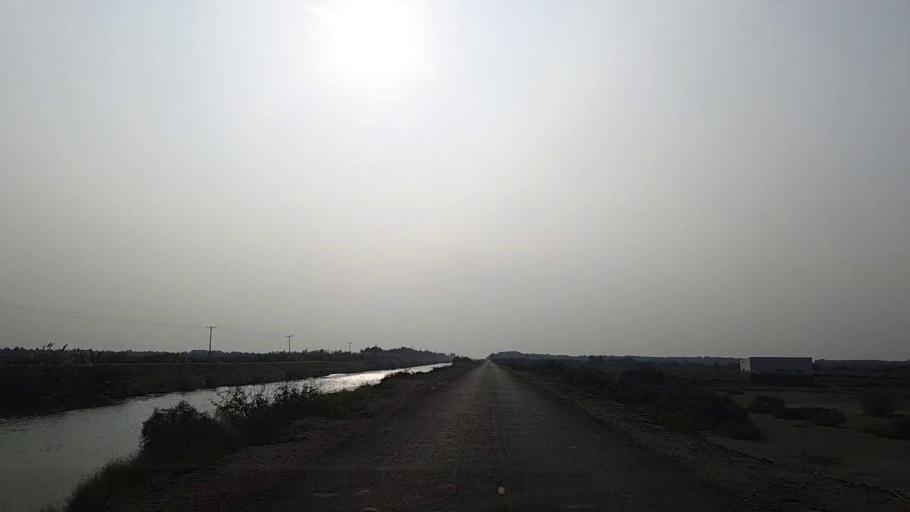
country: PK
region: Sindh
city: Mirpur Sakro
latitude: 24.6296
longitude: 67.5742
